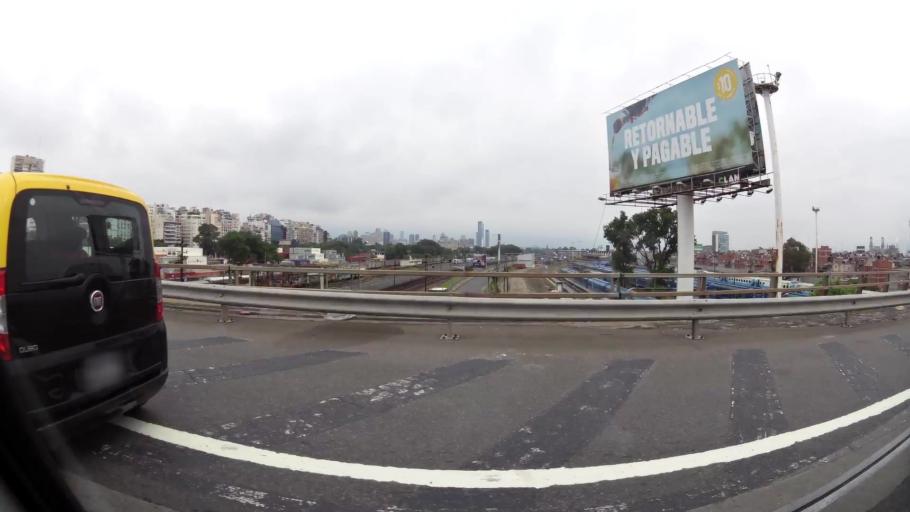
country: AR
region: Buenos Aires F.D.
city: Retiro
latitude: -34.5865
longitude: -58.3806
